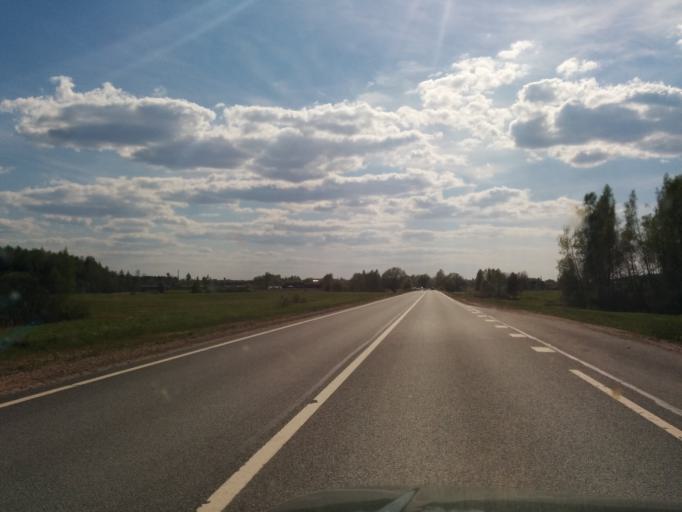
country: LV
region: Krimulda
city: Ragana
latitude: 57.1933
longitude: 24.7354
